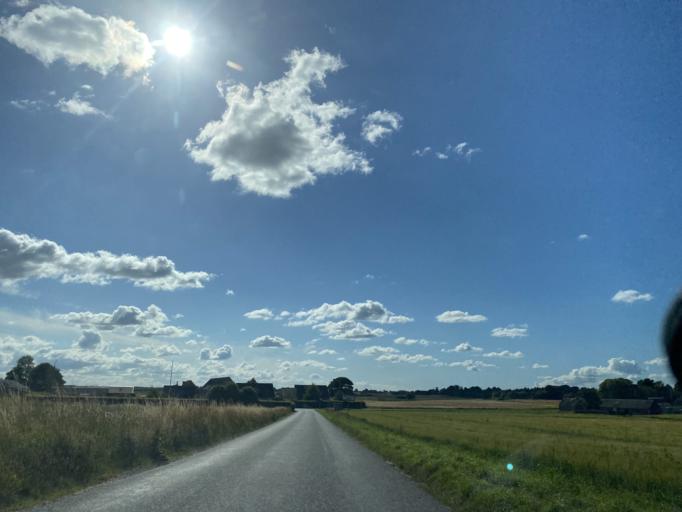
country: DK
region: Central Jutland
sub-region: Viborg Kommune
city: Bjerringbro
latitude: 56.3391
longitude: 9.6871
